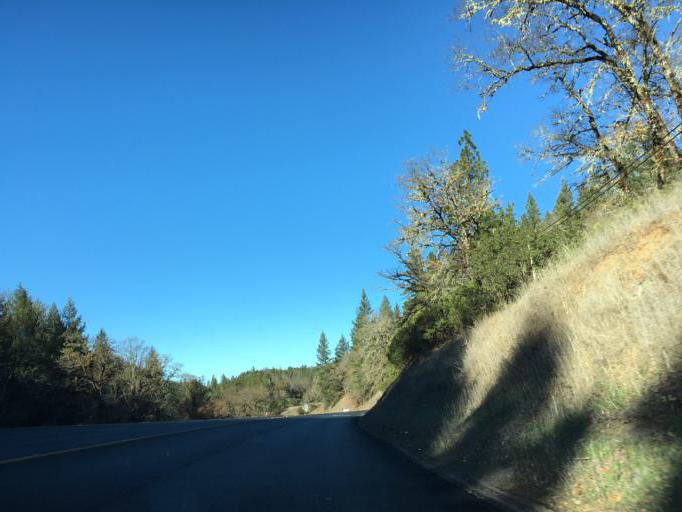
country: US
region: California
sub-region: Mendocino County
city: Laytonville
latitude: 39.7552
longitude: -123.5370
